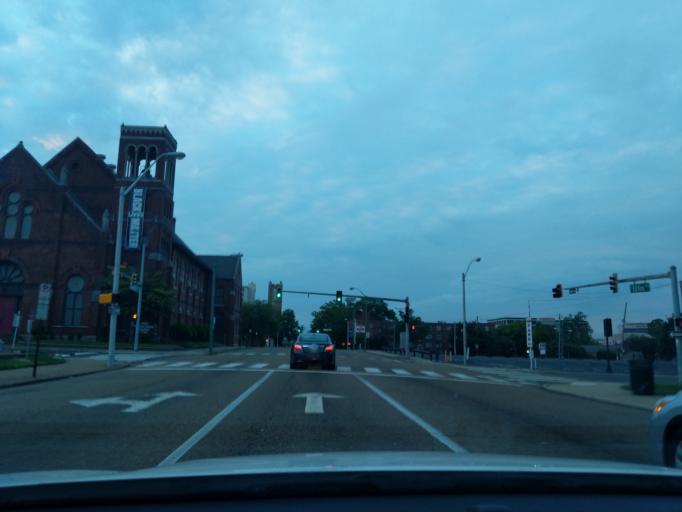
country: US
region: Tennessee
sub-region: Shelby County
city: Memphis
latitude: 35.1491
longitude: -90.0485
